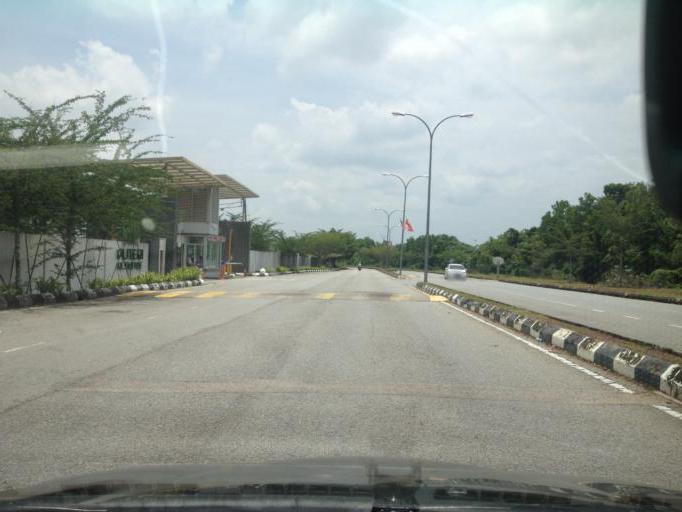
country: MY
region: Kedah
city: Sungai Petani
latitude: 5.6098
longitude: 100.5465
